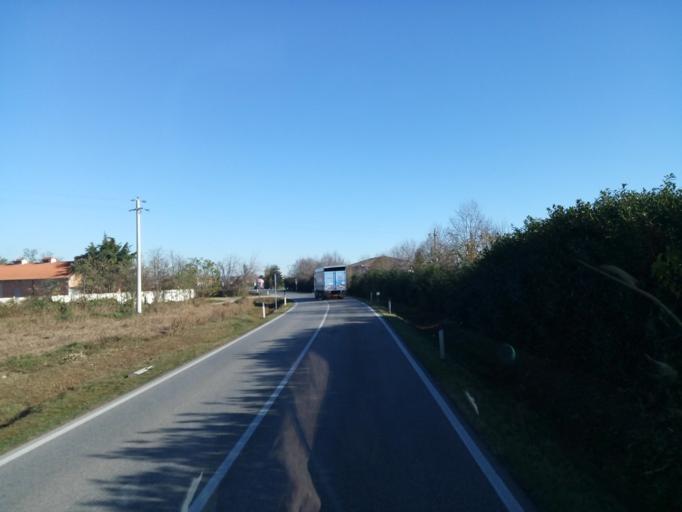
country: IT
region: Veneto
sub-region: Provincia di Treviso
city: Valla
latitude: 45.7139
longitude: 11.9428
